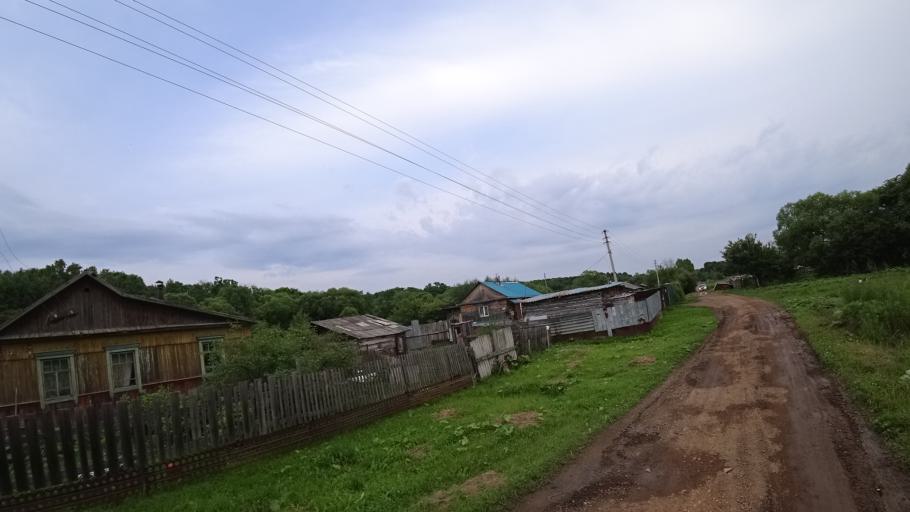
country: RU
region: Primorskiy
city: Novosysoyevka
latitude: 44.2373
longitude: 133.3792
